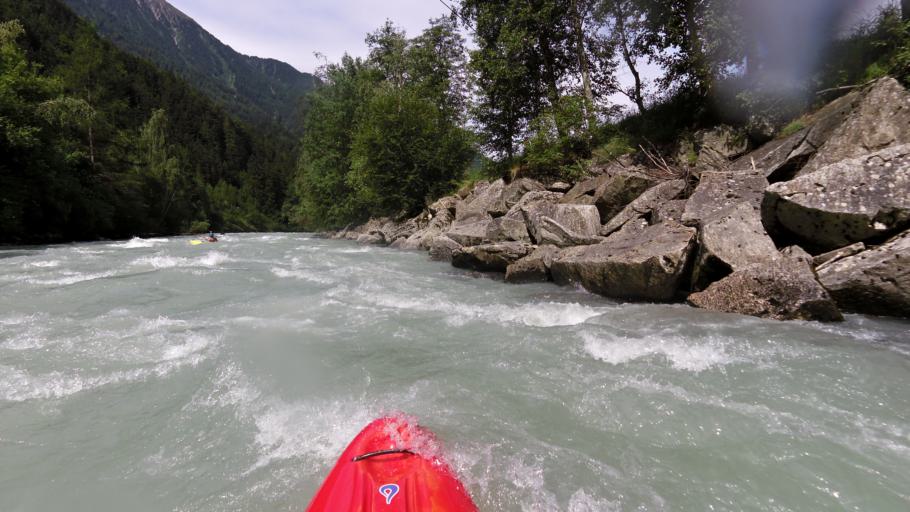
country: AT
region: Tyrol
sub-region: Politischer Bezirk Imst
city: Oetz
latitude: 47.2022
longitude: 10.8906
